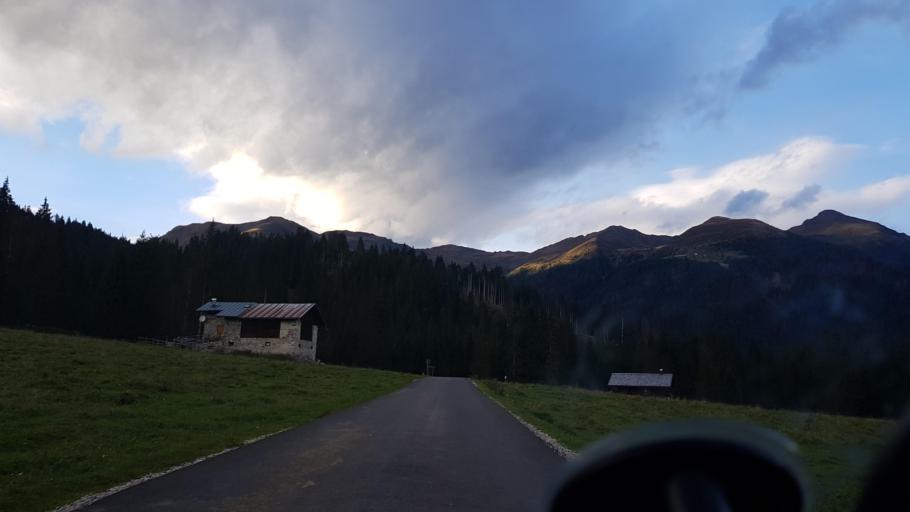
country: IT
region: Veneto
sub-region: Provincia di Belluno
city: San Pietro di Cadore
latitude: 46.6134
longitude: 12.6243
